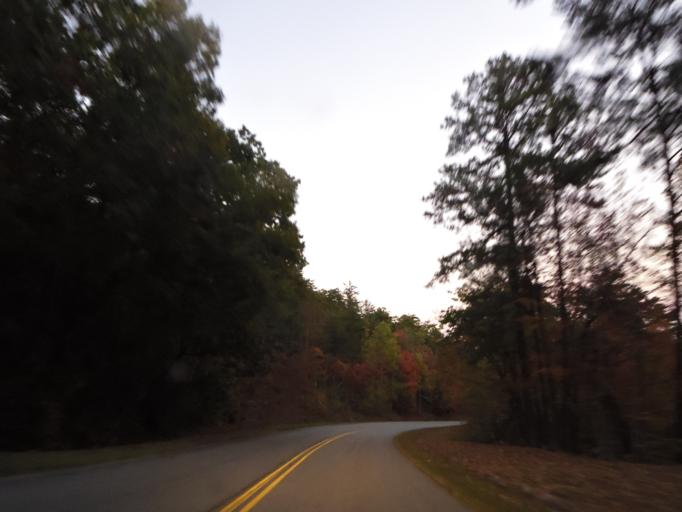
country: US
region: Tennessee
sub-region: Blount County
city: Wildwood
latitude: 35.7036
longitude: -83.8664
